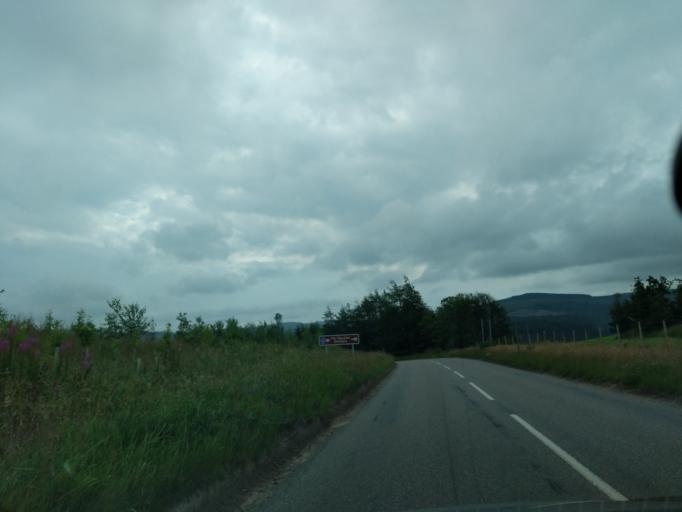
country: GB
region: Scotland
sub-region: Moray
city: Rothes
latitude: 57.4907
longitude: -3.2089
